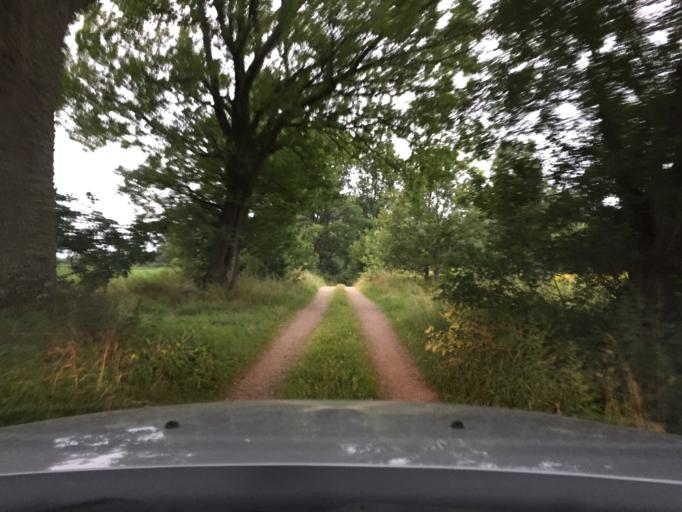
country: SE
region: Skane
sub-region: Hassleholms Kommun
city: Sosdala
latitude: 56.0408
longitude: 13.6911
